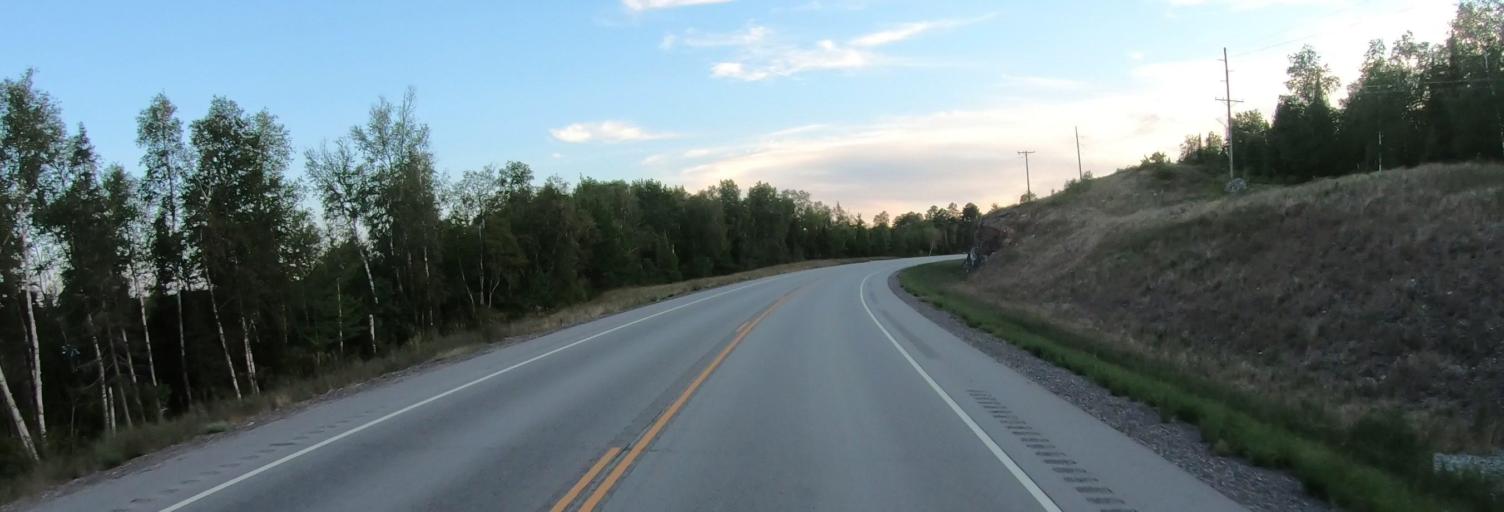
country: US
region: Minnesota
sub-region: Saint Louis County
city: Babbitt
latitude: 47.8538
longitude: -92.0814
